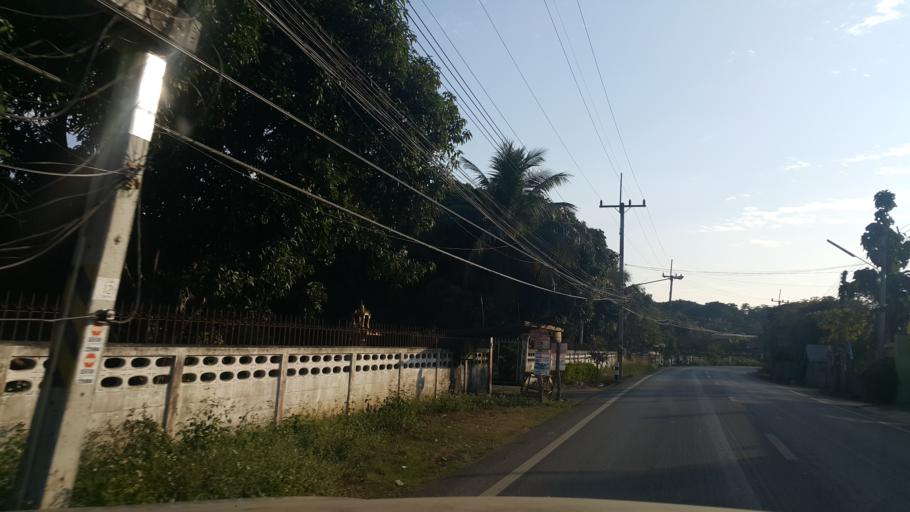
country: TH
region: Lampang
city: Ko Kha
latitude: 18.1105
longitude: 99.3429
